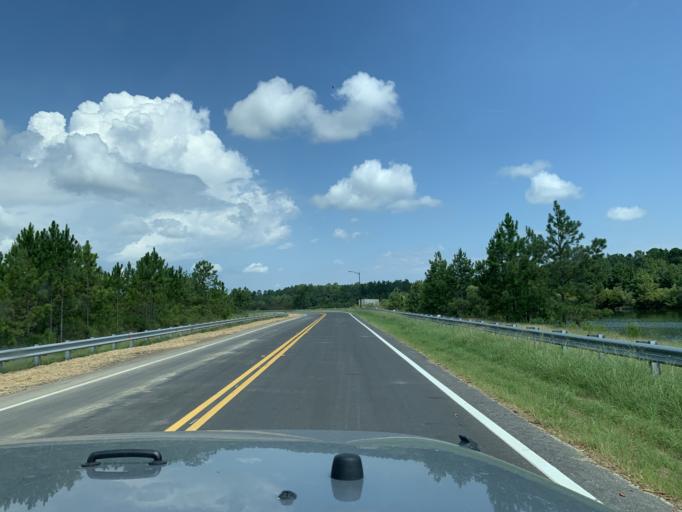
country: US
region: Georgia
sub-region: Chatham County
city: Bloomingdale
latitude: 32.1003
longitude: -81.3755
